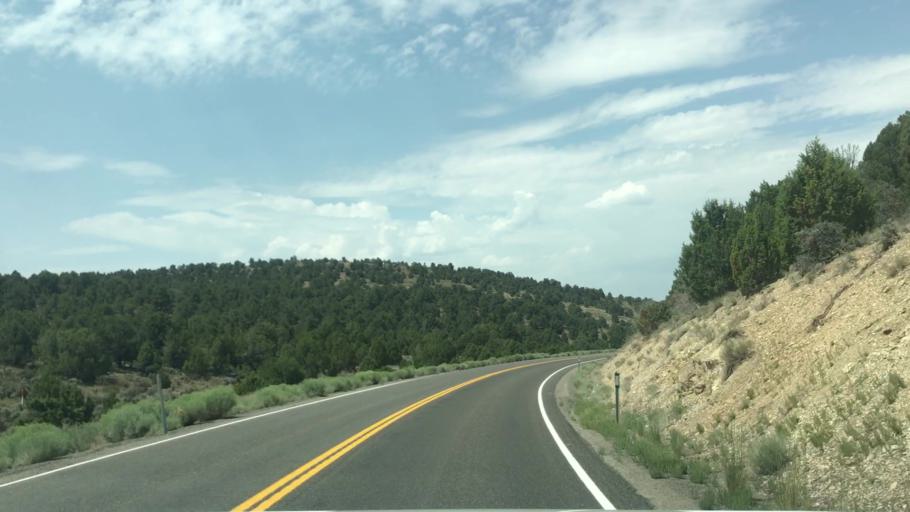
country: US
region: Nevada
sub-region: Eureka County
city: Eureka
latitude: 39.3957
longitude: -115.4777
